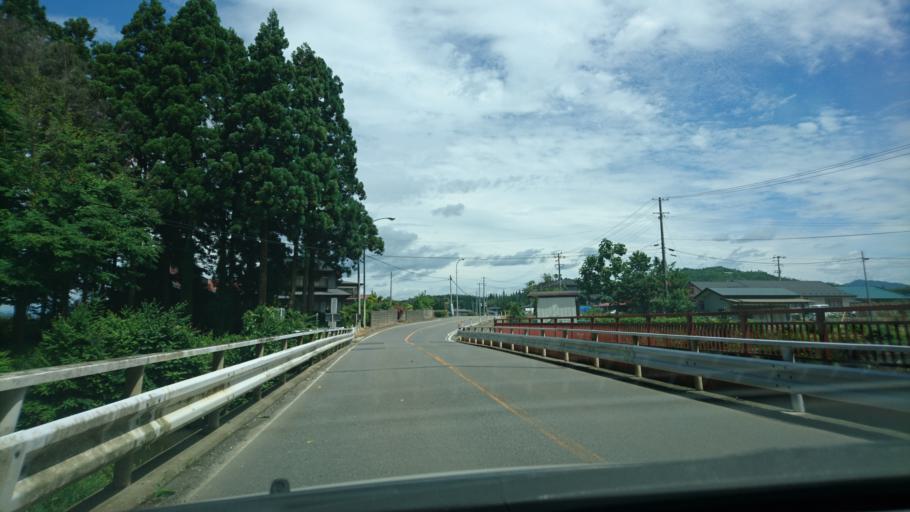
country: JP
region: Iwate
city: Hanamaki
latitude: 39.5193
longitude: 141.1940
